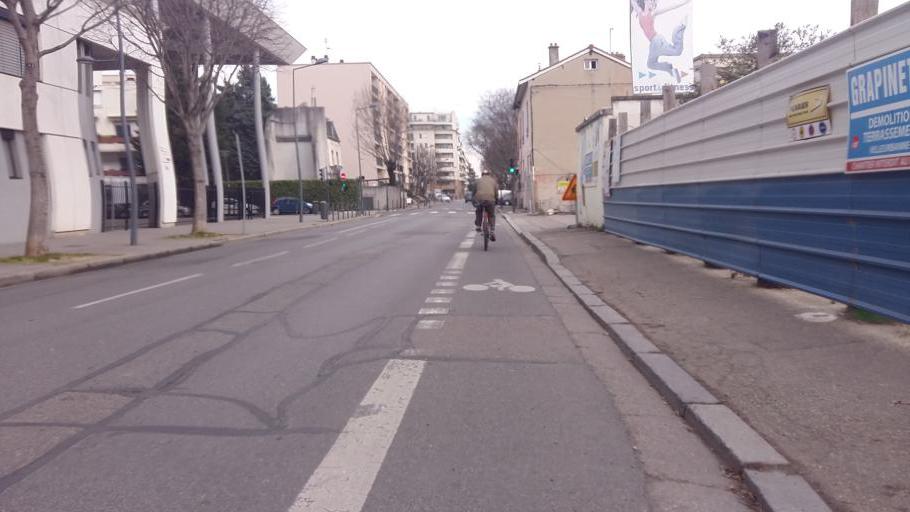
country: FR
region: Rhone-Alpes
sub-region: Departement du Rhone
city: Villeurbanne
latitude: 45.7720
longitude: 4.8768
